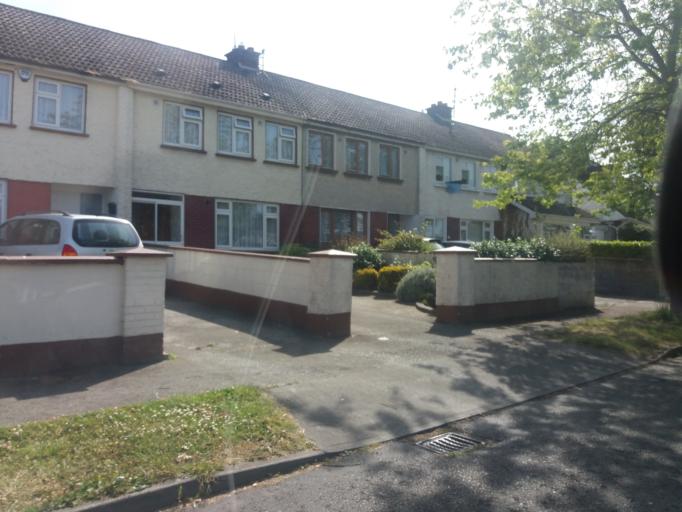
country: IE
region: Leinster
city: Lusk
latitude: 53.5261
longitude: -6.1742
